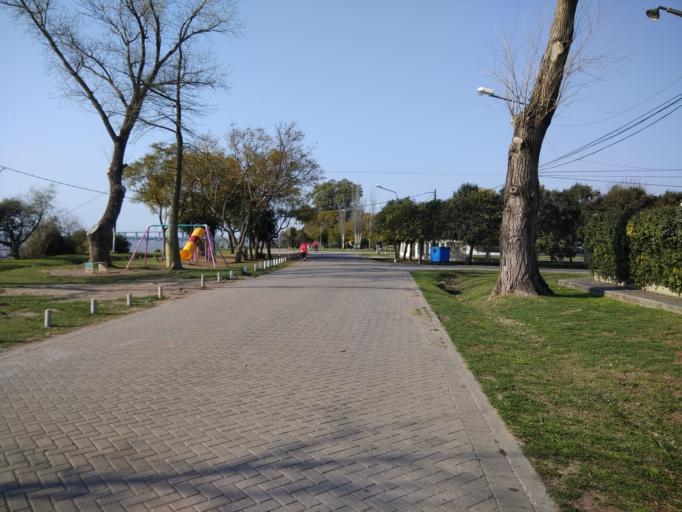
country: AR
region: Santa Fe
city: Granadero Baigorria
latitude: -32.8483
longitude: -60.6969
